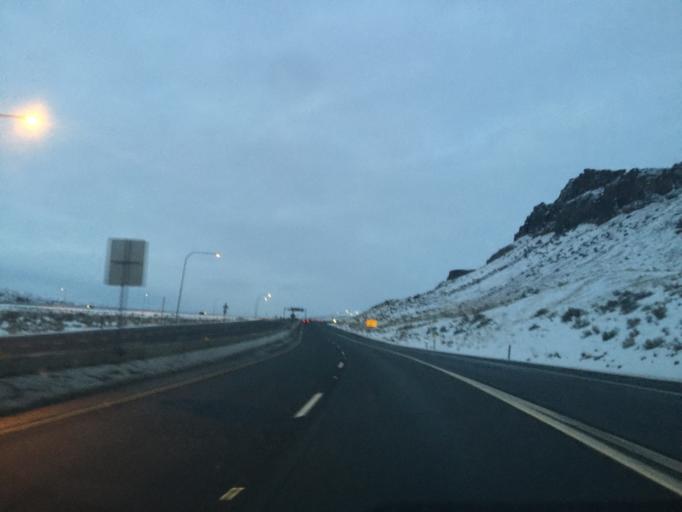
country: US
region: Washington
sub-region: Grant County
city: Mattawa
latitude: 46.9474
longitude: -119.9607
